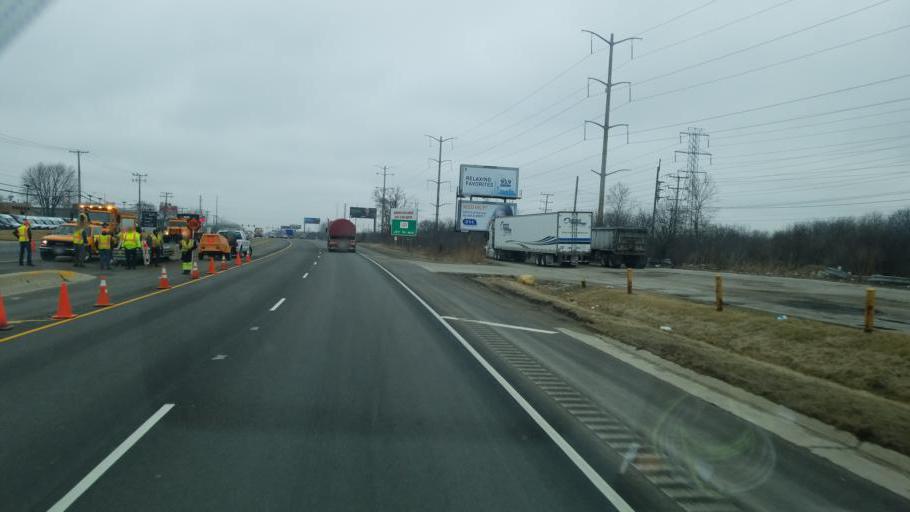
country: US
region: Illinois
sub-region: Lake County
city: Knollwood
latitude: 42.3045
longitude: -87.8756
